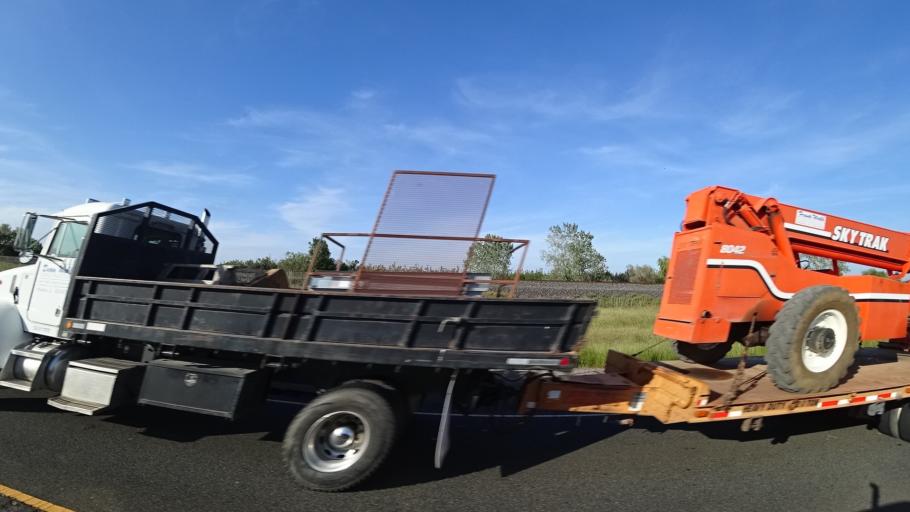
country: US
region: California
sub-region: Placer County
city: Sheridan
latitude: 38.9927
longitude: -121.3941
